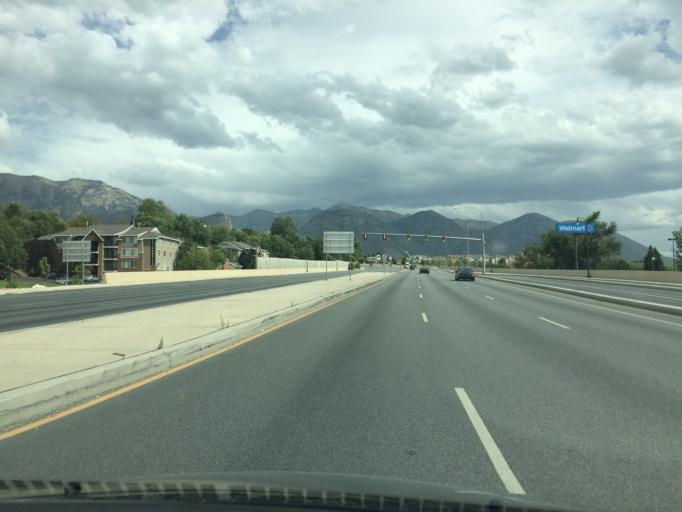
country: US
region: Utah
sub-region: Utah County
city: Orem
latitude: 40.2749
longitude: -111.7132
